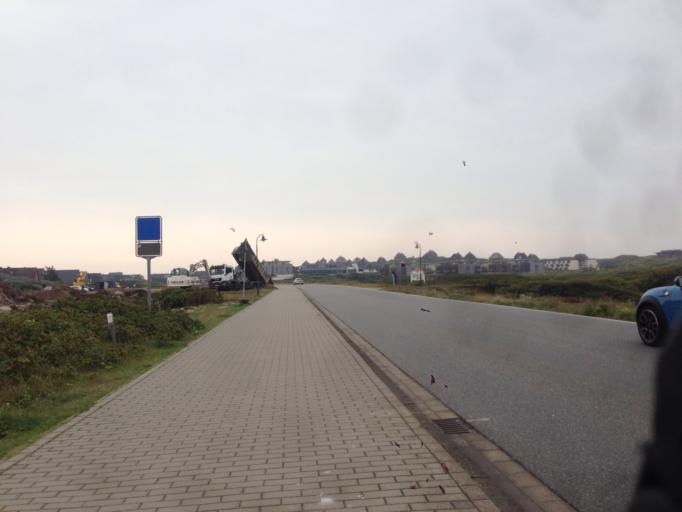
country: DE
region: Schleswig-Holstein
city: Norddorf
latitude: 54.7616
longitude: 8.2865
